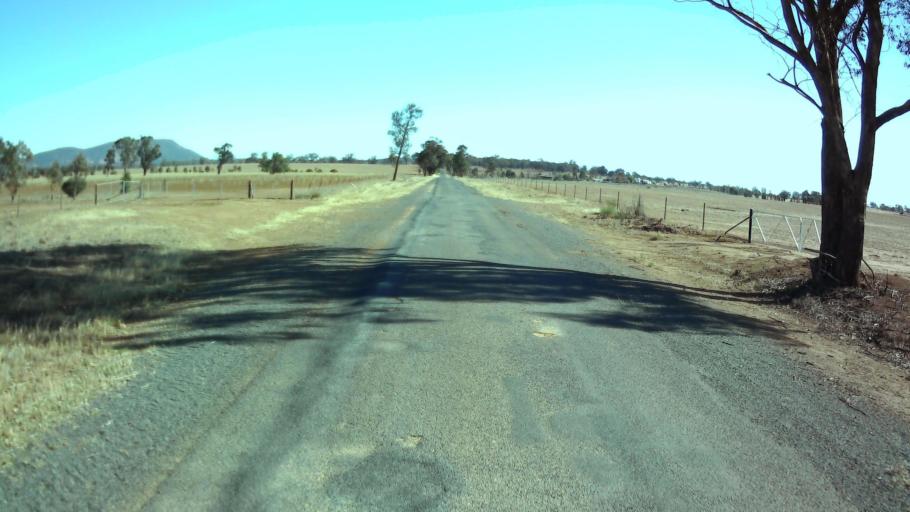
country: AU
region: New South Wales
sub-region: Weddin
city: Grenfell
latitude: -33.7993
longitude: 147.9560
